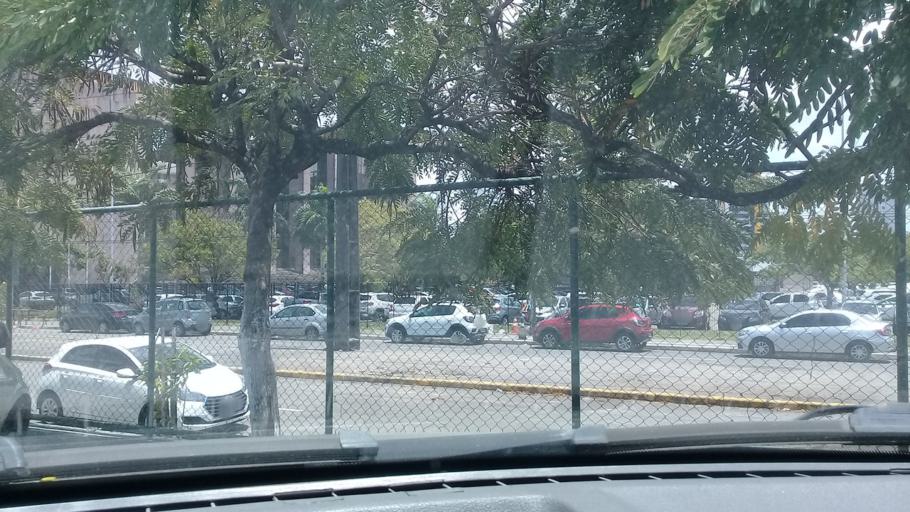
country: BR
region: Pernambuco
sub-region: Recife
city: Recife
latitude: -8.0717
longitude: -34.8939
